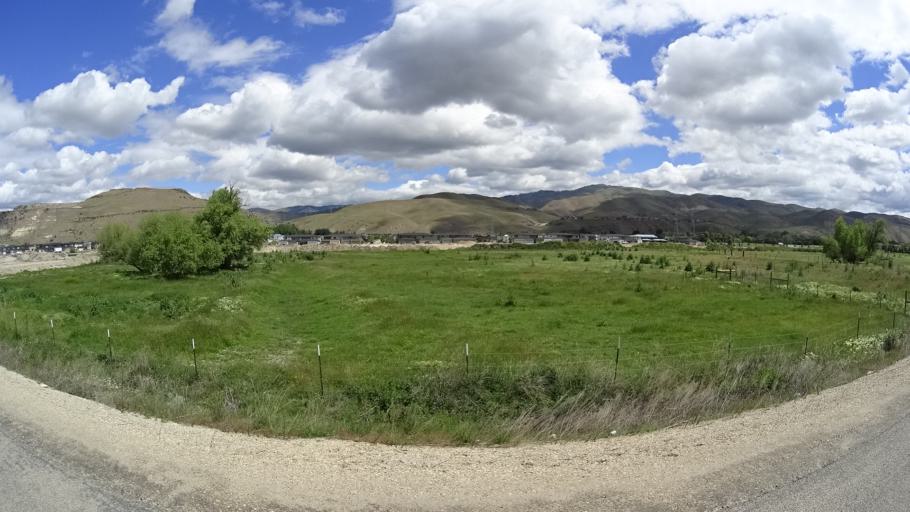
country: US
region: Idaho
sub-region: Ada County
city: Boise
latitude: 43.5702
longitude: -116.1328
